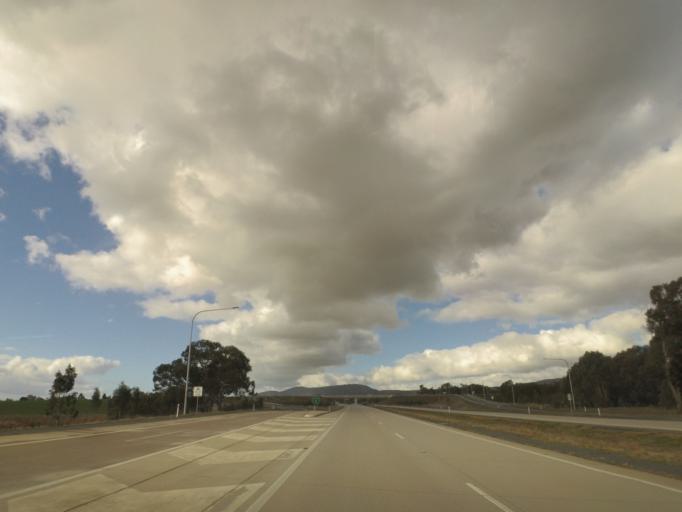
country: AU
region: New South Wales
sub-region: Greater Hume Shire
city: Holbrook
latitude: -35.7047
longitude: 147.3185
